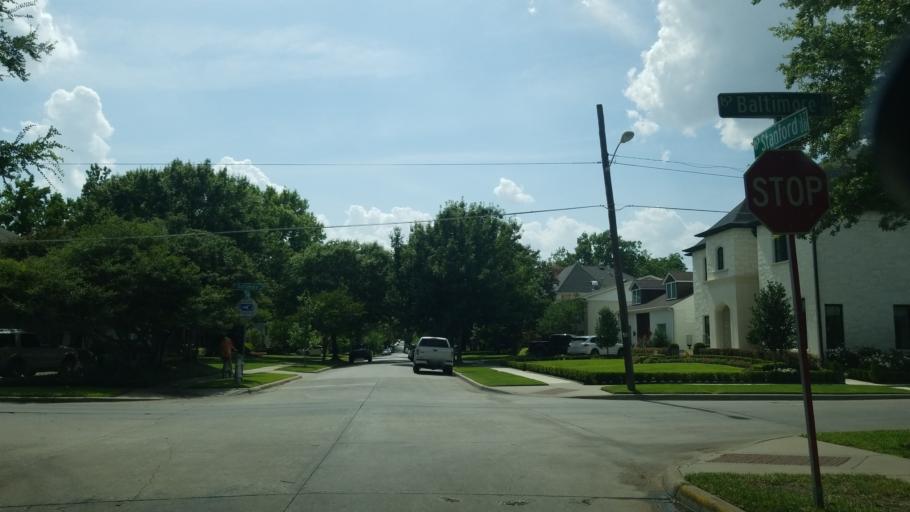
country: US
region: Texas
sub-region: Dallas County
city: University Park
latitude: 32.8530
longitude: -96.7964
